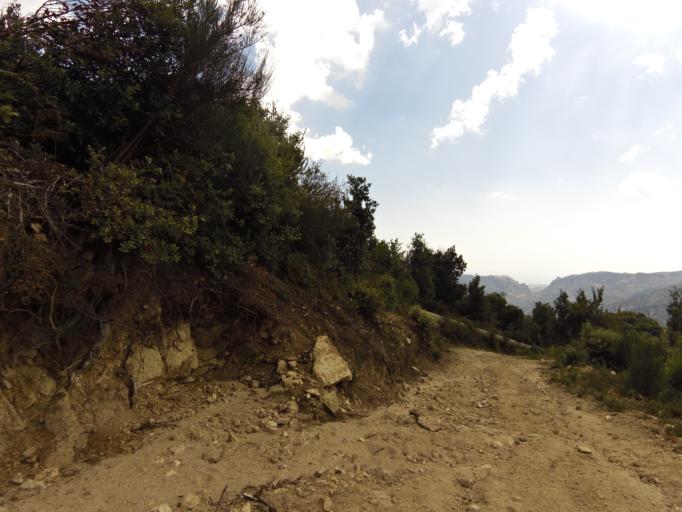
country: IT
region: Calabria
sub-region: Provincia di Reggio Calabria
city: Bivongi
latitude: 38.5065
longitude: 16.3971
